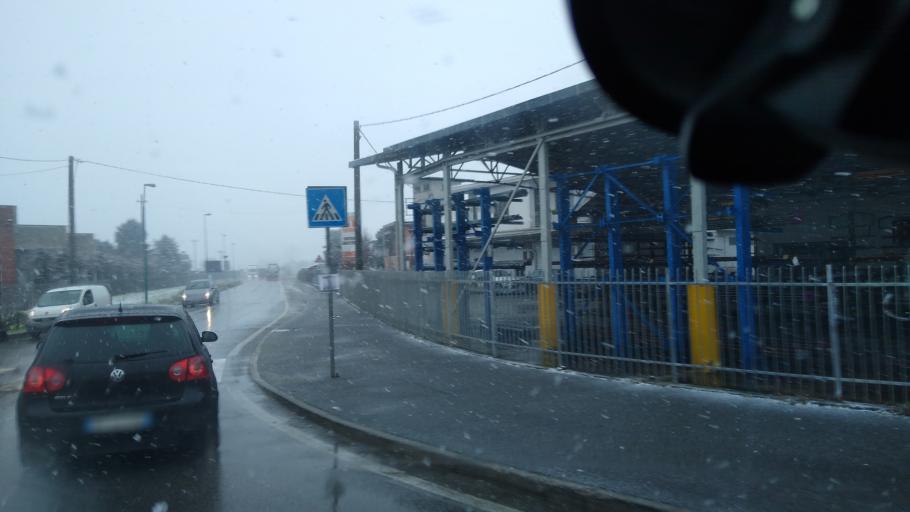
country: IT
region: Lombardy
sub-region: Provincia di Bergamo
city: Bariano
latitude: 45.5121
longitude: 9.6999
